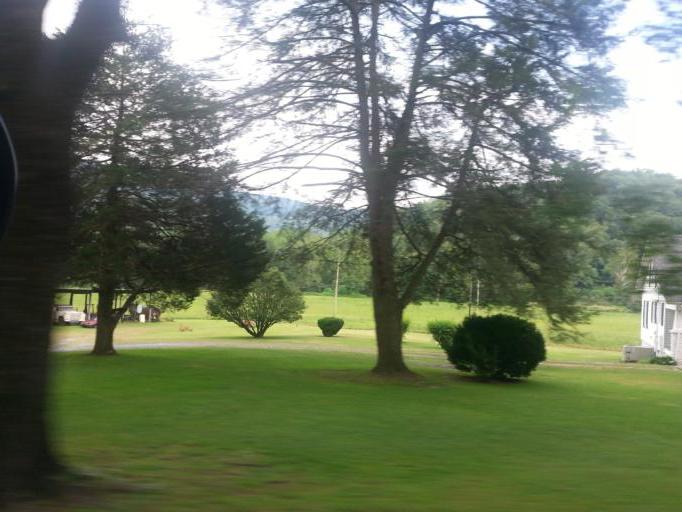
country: US
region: Tennessee
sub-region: Roane County
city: Oliver Springs
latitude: 36.1690
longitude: -84.3546
